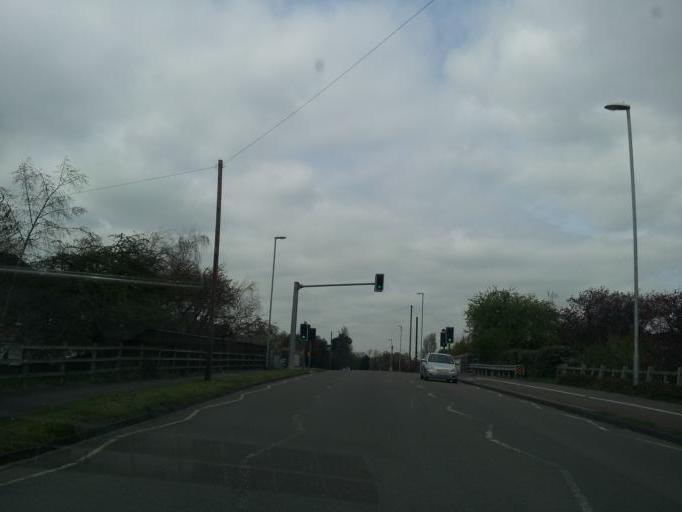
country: GB
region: England
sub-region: Cambridgeshire
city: Grantchester
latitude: 52.1690
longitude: 0.1160
